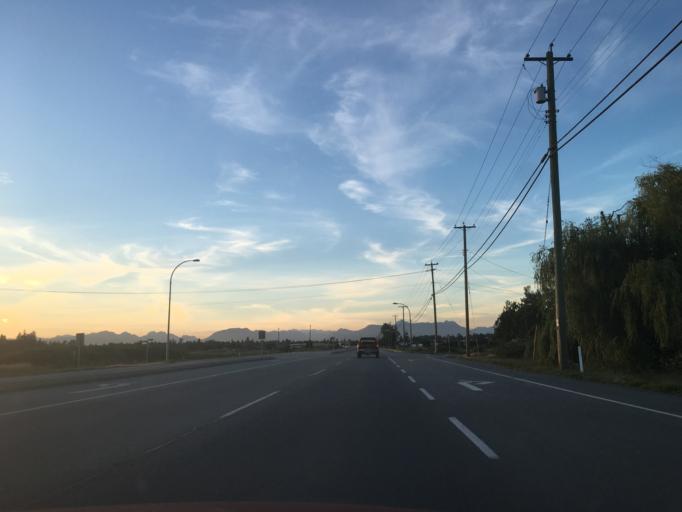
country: CA
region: British Columbia
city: Langley
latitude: 49.0887
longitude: -122.7351
